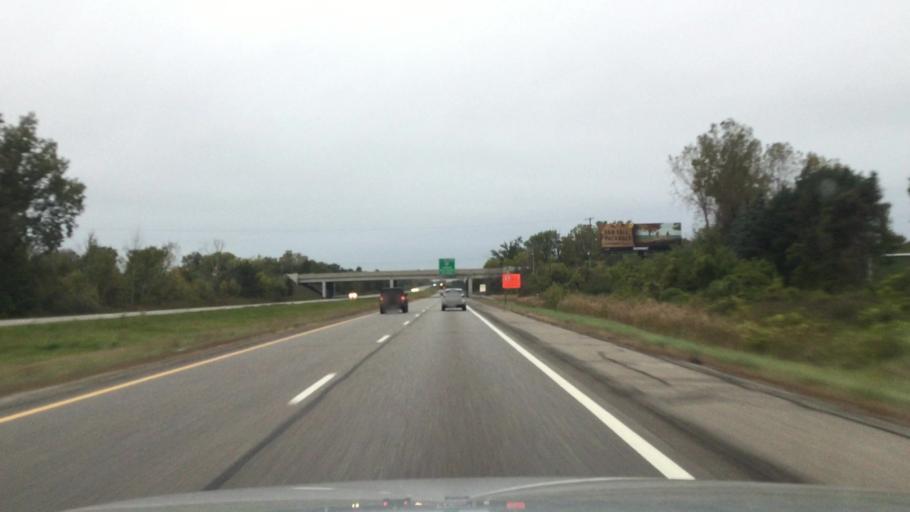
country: US
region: Michigan
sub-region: Genesee County
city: Flint
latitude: 42.9426
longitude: -83.7108
